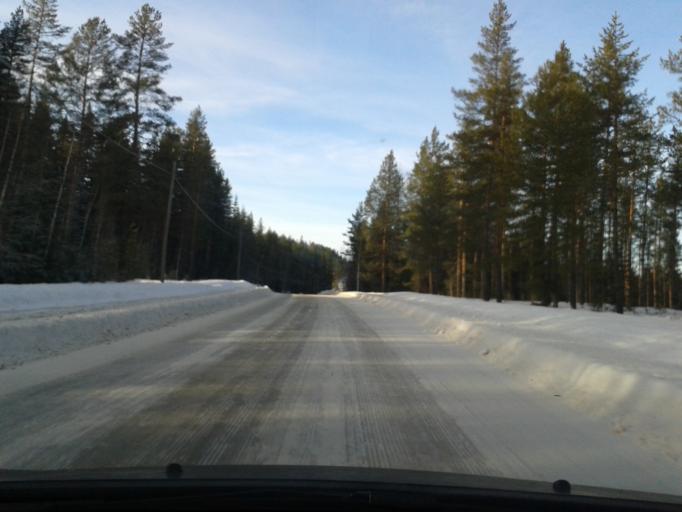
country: SE
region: Vaesternorrland
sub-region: OErnskoeldsviks Kommun
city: Bredbyn
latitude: 63.6664
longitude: 17.8326
